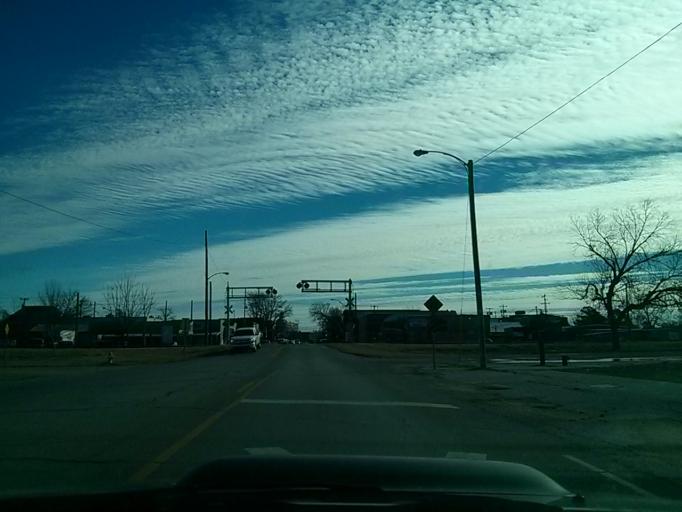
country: US
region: Oklahoma
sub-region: Tulsa County
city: Jenks
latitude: 36.0226
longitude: -95.9716
